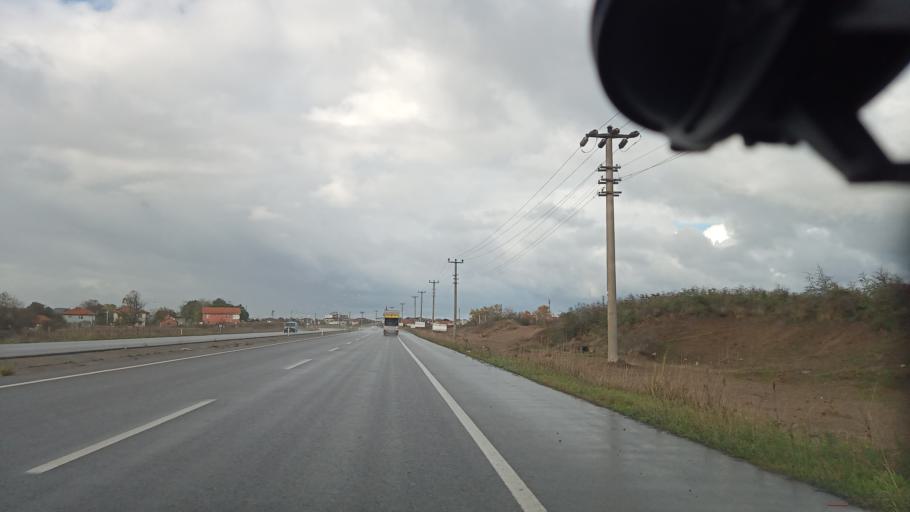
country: TR
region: Sakarya
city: Karasu
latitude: 41.0860
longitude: 30.7531
